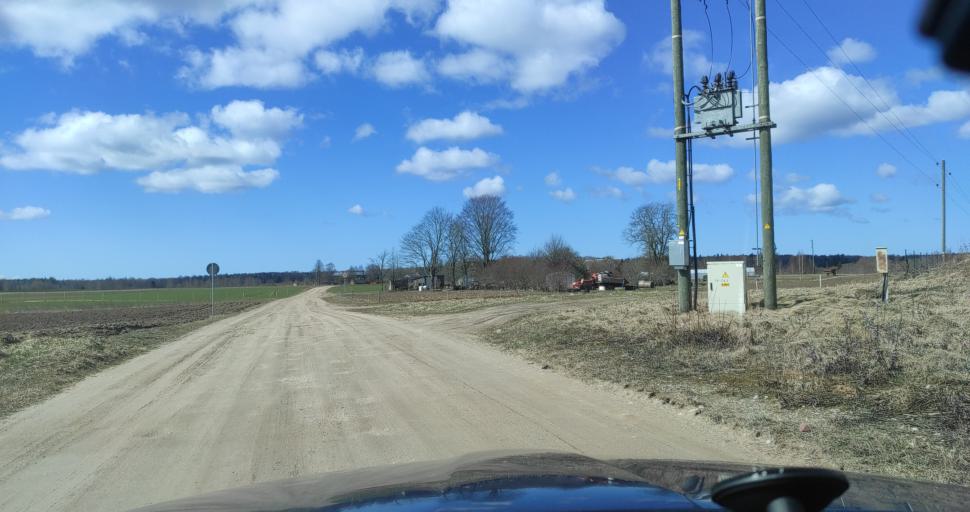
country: LV
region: Kuldigas Rajons
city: Kuldiga
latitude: 56.9560
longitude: 21.9146
